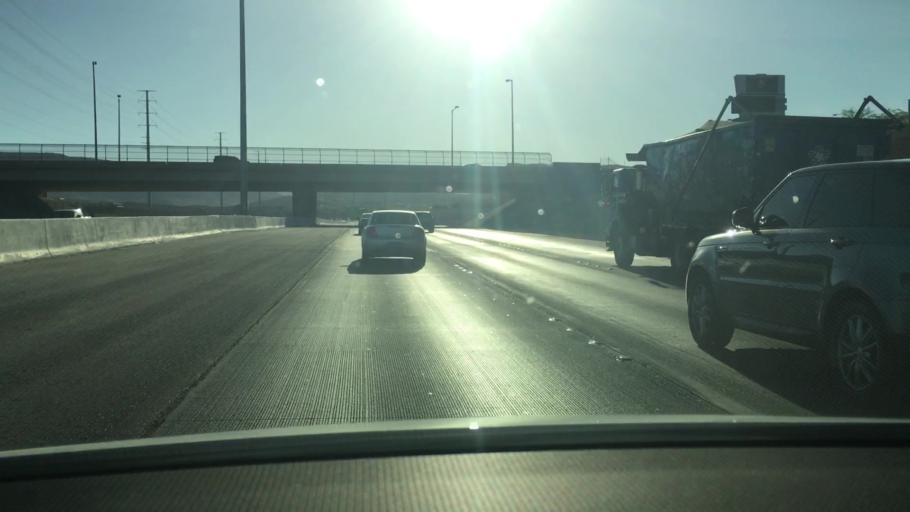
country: US
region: Nevada
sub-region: Clark County
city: Summerlin South
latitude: 36.1188
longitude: -115.3136
